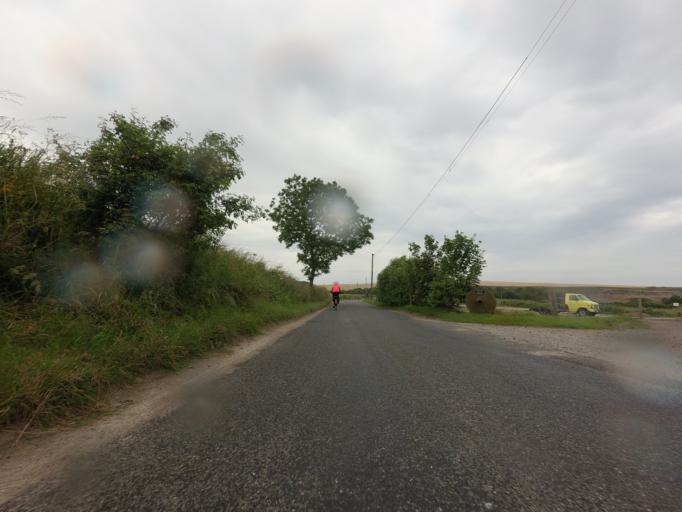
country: GB
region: Scotland
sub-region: Aberdeenshire
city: Portsoy
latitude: 57.6757
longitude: -2.6477
